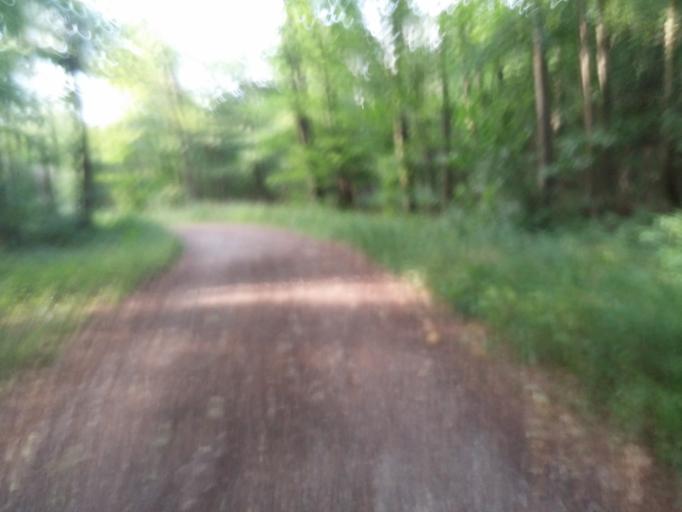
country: DE
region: Bavaria
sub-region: Upper Bavaria
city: Vaterstetten
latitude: 48.1193
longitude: 11.7548
